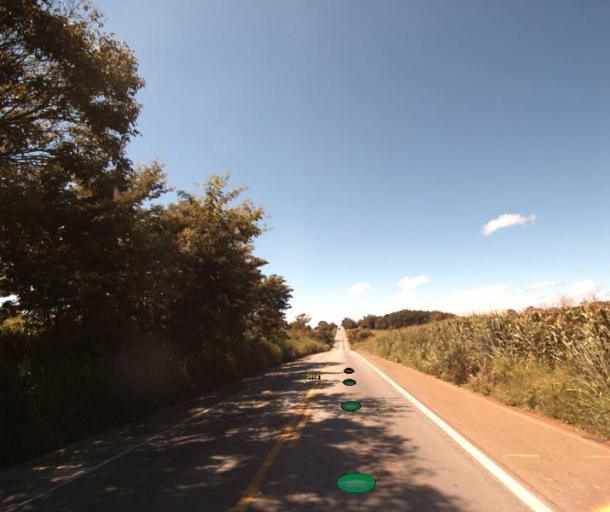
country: BR
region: Goias
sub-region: Jaragua
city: Jaragua
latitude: -15.6185
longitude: -49.3942
